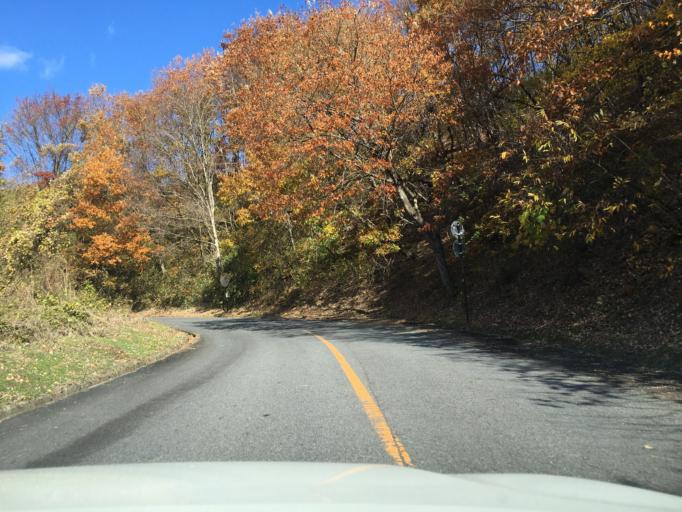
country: JP
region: Fukushima
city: Miharu
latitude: 37.4565
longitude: 140.5050
